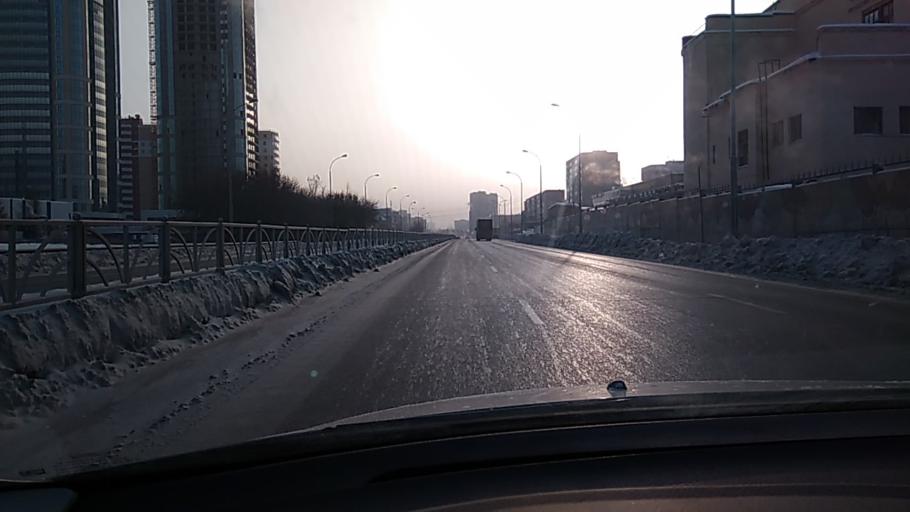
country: RU
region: Sverdlovsk
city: Yekaterinburg
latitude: 56.8154
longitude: 60.6284
